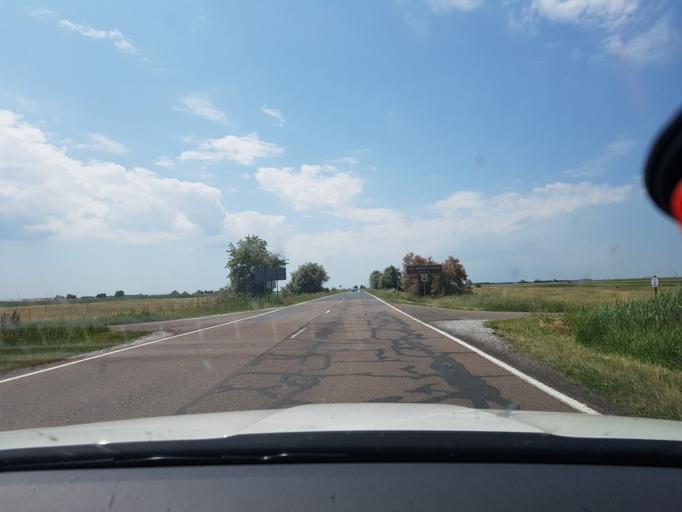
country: HU
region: Hajdu-Bihar
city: Egyek
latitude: 47.5718
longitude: 20.9889
